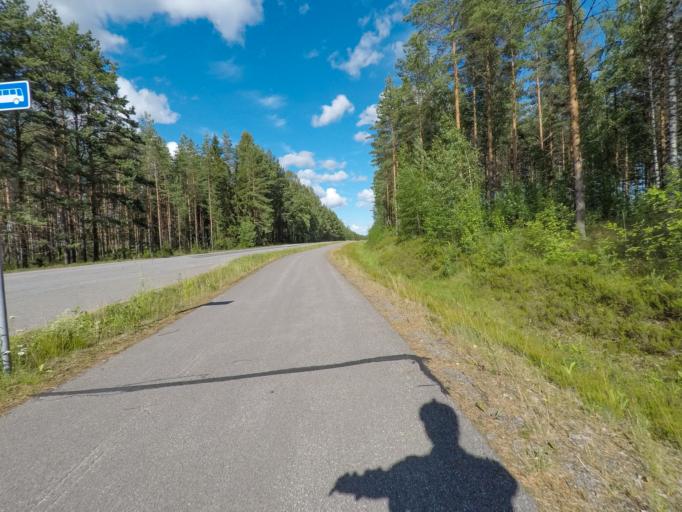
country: FI
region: South Karelia
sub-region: Lappeenranta
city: Joutseno
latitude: 61.1495
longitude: 28.5540
